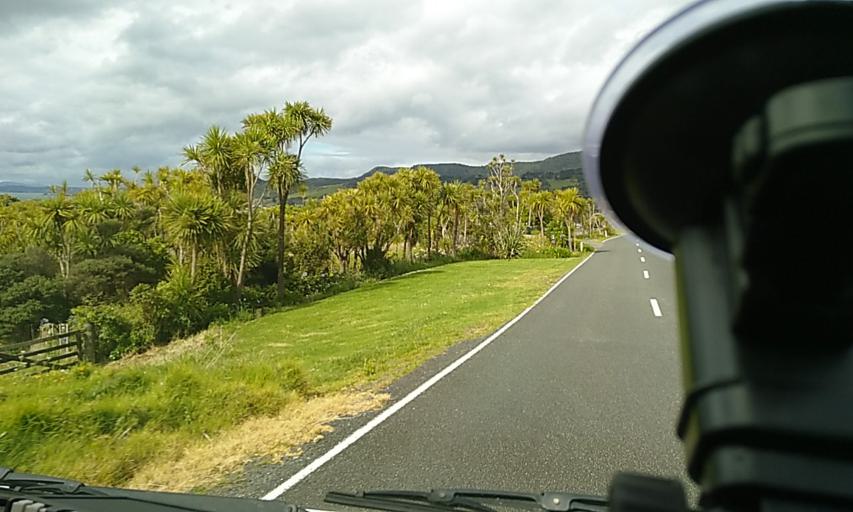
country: NZ
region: Northland
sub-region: Far North District
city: Ahipara
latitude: -35.5381
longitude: 173.3755
